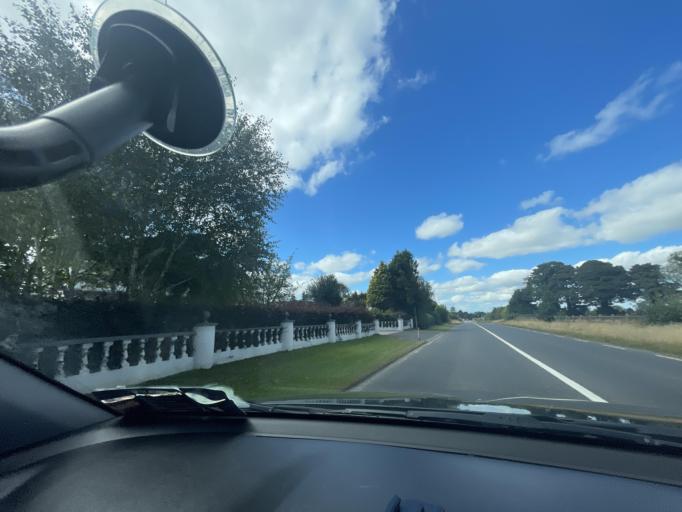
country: IE
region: Leinster
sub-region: An Mhi
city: Dunshaughlin
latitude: 53.5196
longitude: -6.6442
